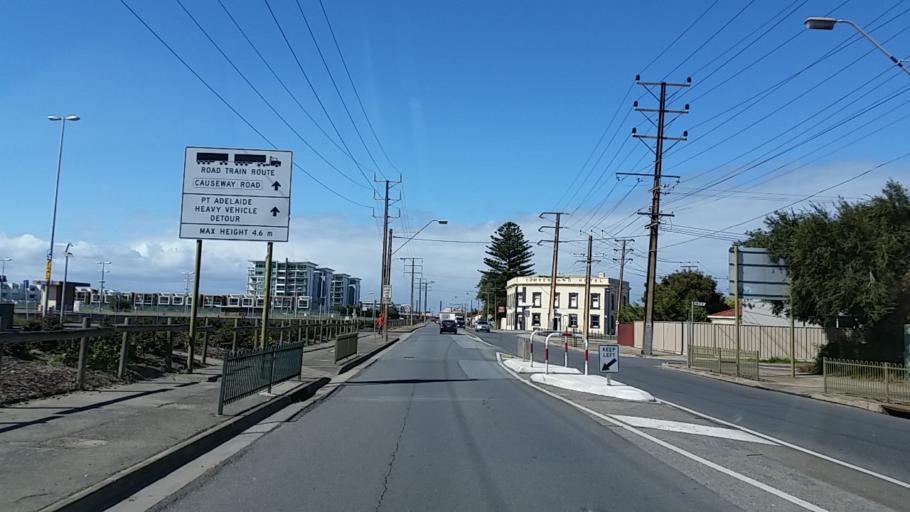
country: AU
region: South Australia
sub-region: Port Adelaide Enfield
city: Birkenhead
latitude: -34.8416
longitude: 138.4928
